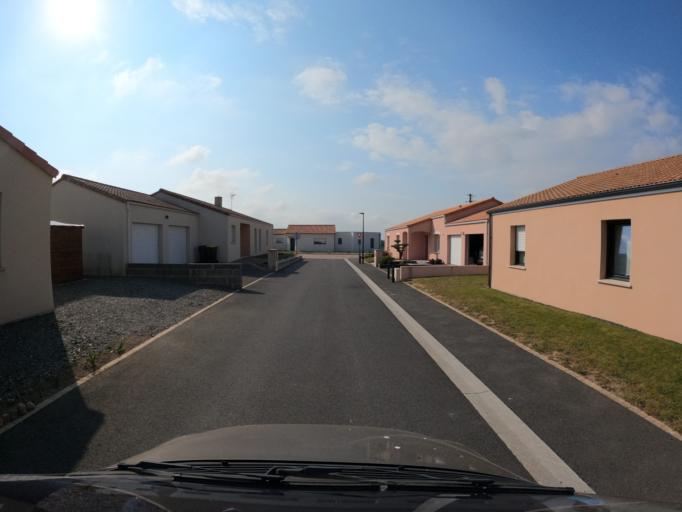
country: FR
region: Pays de la Loire
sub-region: Departement de Maine-et-Loire
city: Torfou
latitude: 47.0313
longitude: -1.1254
